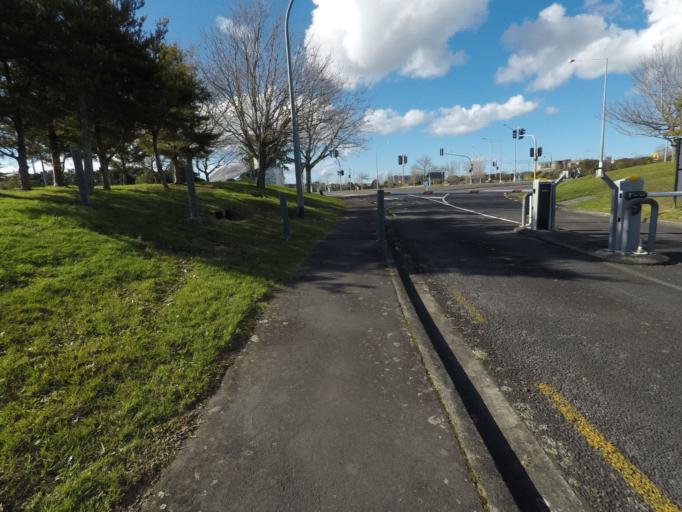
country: NZ
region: Auckland
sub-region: Auckland
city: Rothesay Bay
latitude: -36.7299
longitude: 174.7008
